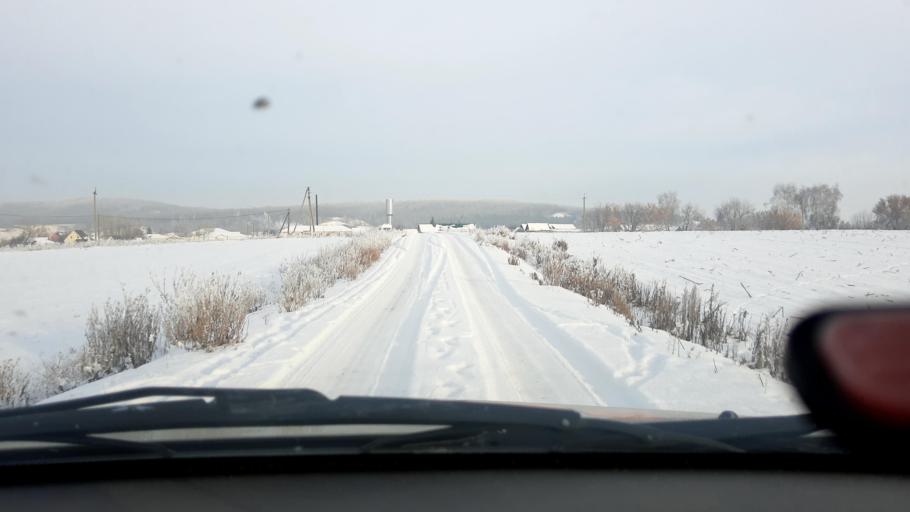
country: RU
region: Bashkortostan
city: Tolbazy
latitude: 54.3537
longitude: 55.8400
